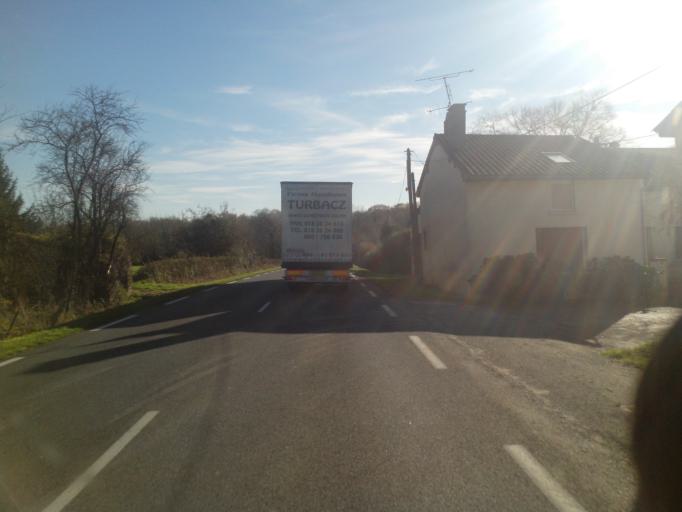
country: FR
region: Limousin
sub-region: Departement de la Haute-Vienne
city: Bussiere-Poitevine
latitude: 46.2130
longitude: 0.9118
